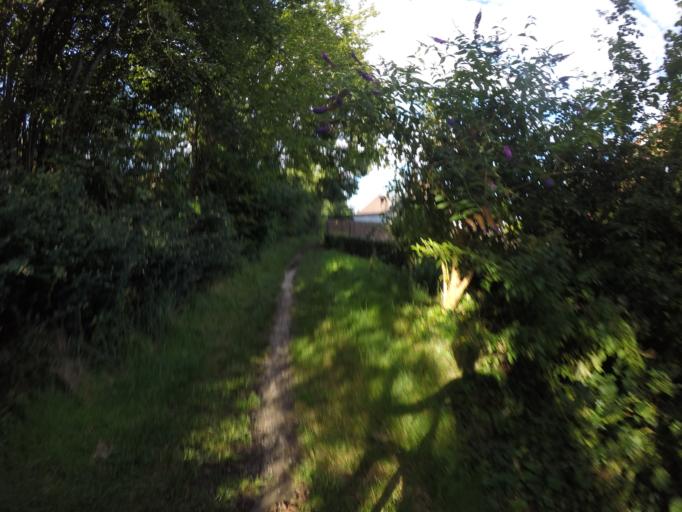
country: DE
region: Bavaria
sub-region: Lower Bavaria
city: Landshut
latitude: 48.5159
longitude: 12.1423
